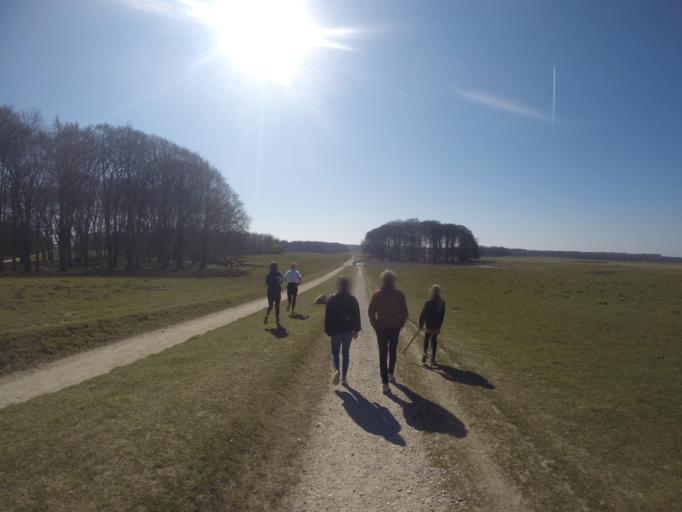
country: DK
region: Capital Region
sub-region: Gentofte Kommune
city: Charlottenlund
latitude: 55.7948
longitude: 12.5708
